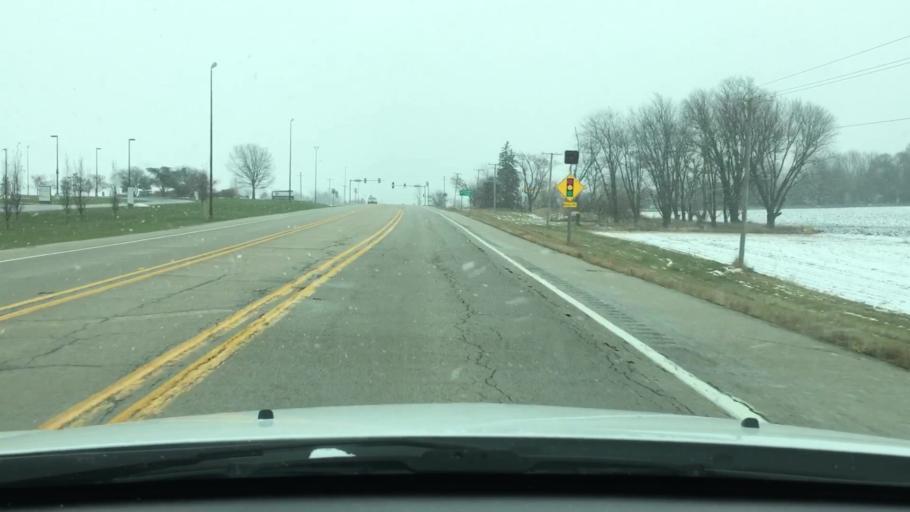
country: US
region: Illinois
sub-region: DeKalb County
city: Malta
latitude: 41.9356
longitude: -88.8802
